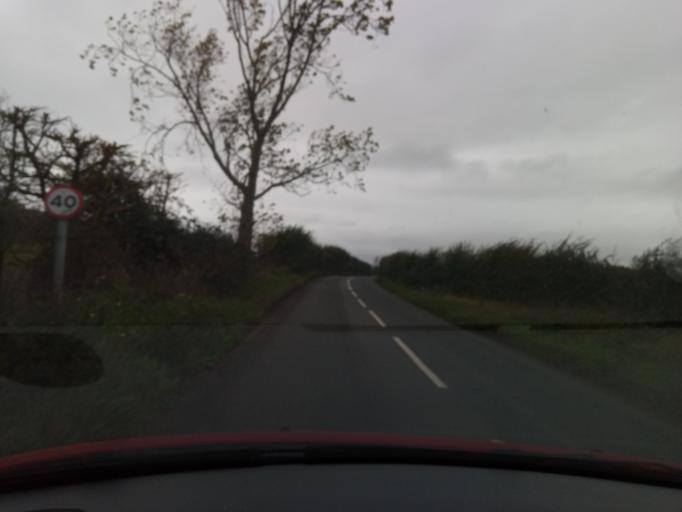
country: GB
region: England
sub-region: Essex
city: Brightlingsea
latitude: 51.7916
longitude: 0.9774
